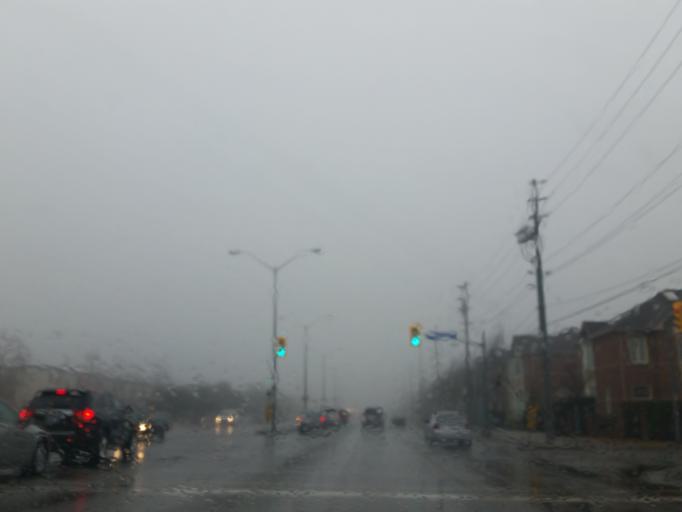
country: CA
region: Ontario
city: Scarborough
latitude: 43.7499
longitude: -79.2059
